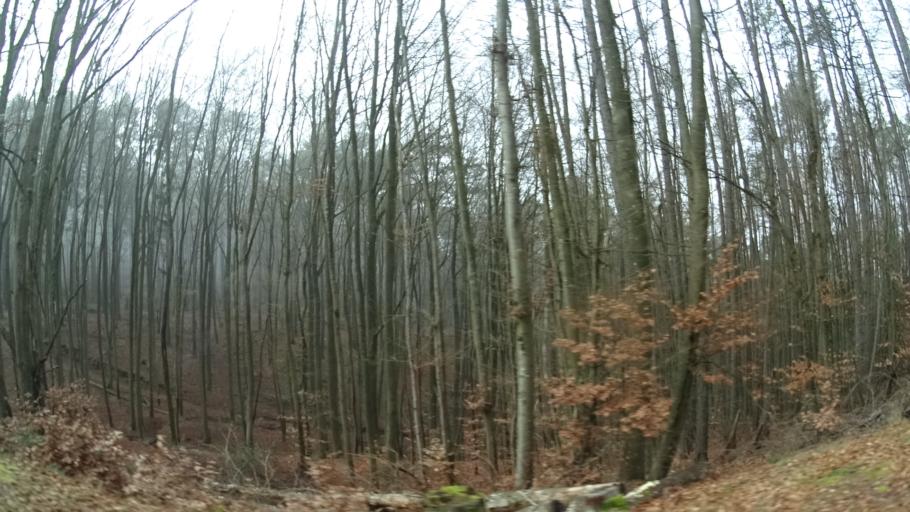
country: DE
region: Rheinland-Pfalz
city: Hochspeyer
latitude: 49.4289
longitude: 7.8895
